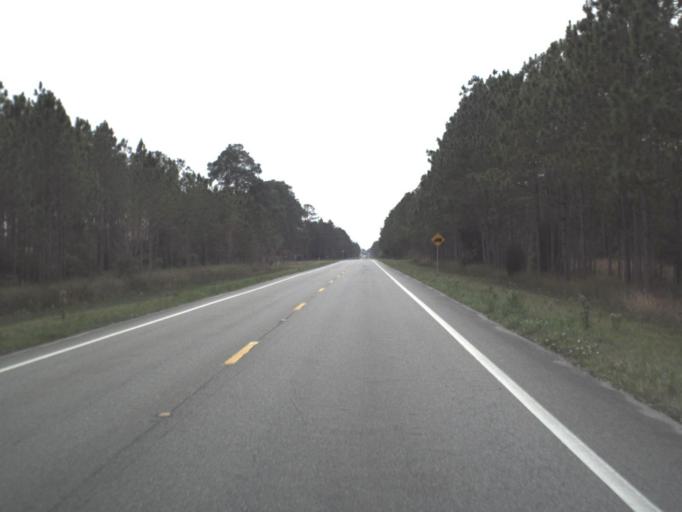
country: US
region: Florida
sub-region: Gulf County
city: Port Saint Joe
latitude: 29.9044
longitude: -85.2085
